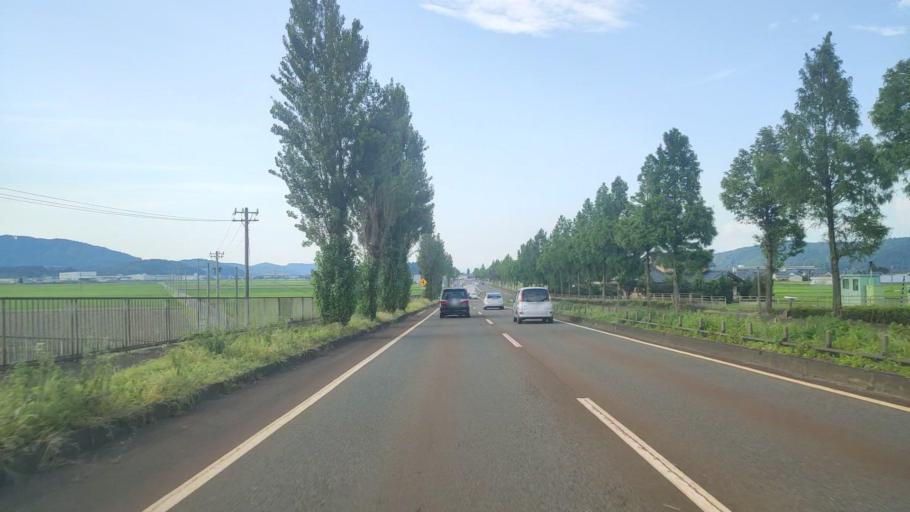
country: JP
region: Fukui
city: Sabae
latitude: 35.9818
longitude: 136.1963
